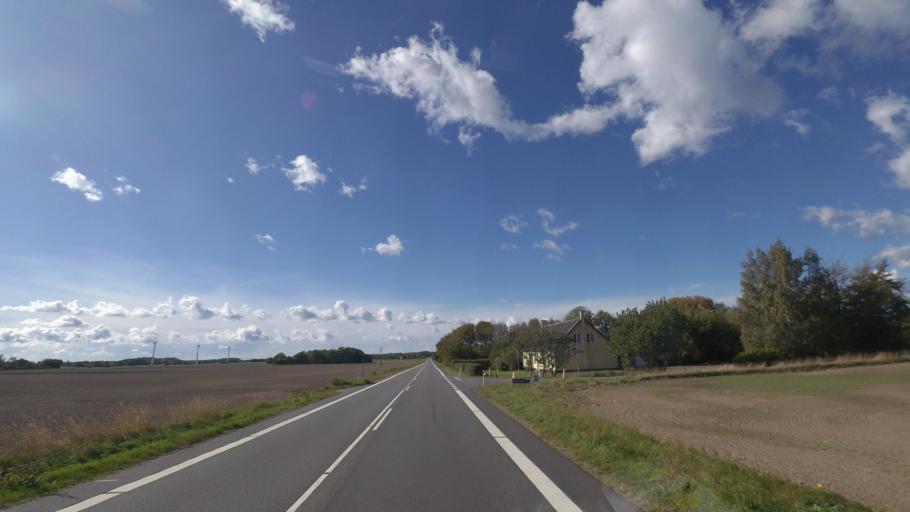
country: DK
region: Capital Region
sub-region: Bornholm Kommune
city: Nexo
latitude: 55.0612
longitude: 15.0674
